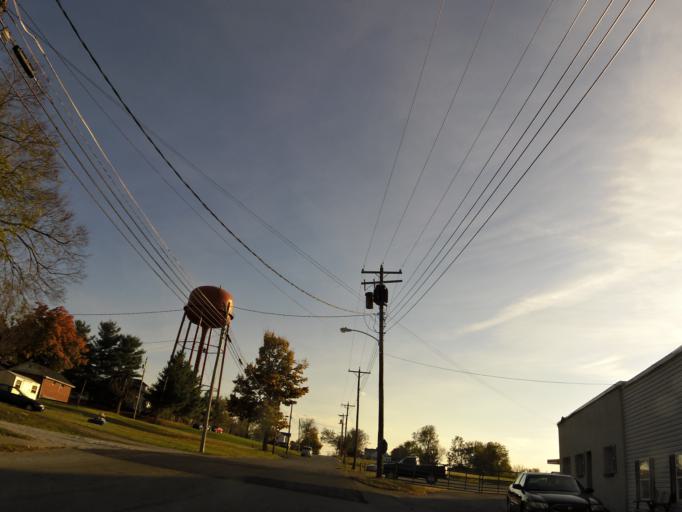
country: US
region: Kentucky
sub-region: Garrard County
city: Lancaster
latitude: 37.6170
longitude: -84.5775
